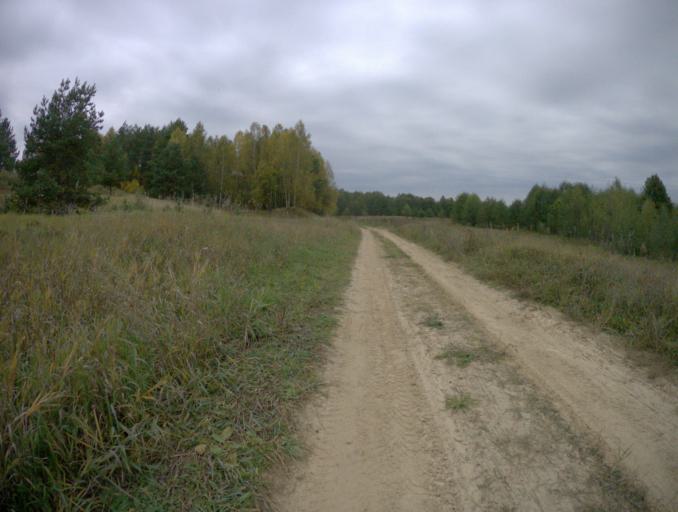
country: RU
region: Vladimir
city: Mstera
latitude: 56.3578
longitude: 41.8684
